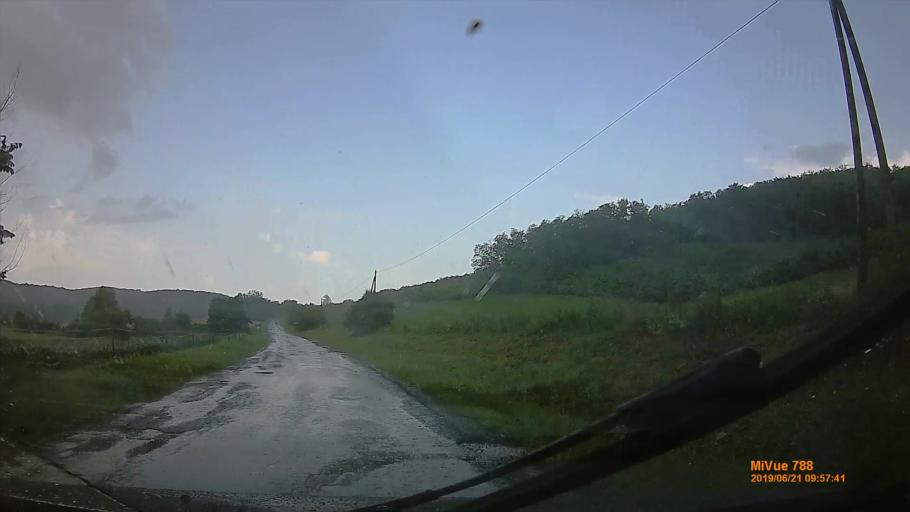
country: HU
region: Baranya
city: Buekkoesd
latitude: 46.2190
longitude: 17.9715
